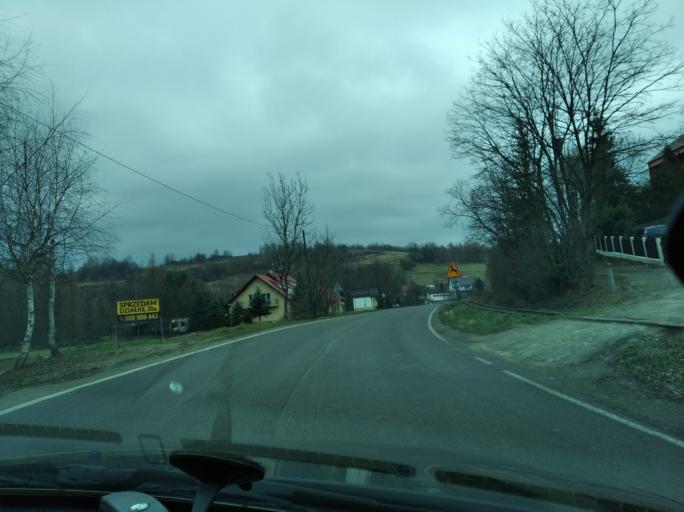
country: PL
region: Subcarpathian Voivodeship
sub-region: Powiat przeworski
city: Jawornik Polski
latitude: 49.9111
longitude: 22.2991
